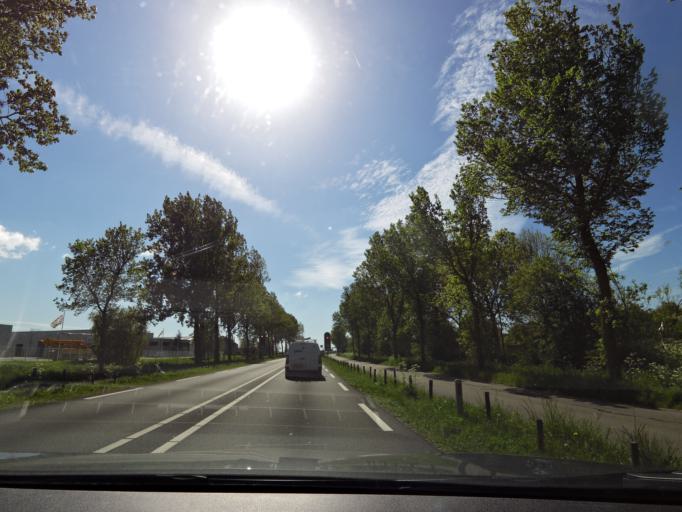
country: NL
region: Zeeland
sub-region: Schouwen-Duiveland
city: Bruinisse
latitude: 51.6470
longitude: 4.0053
